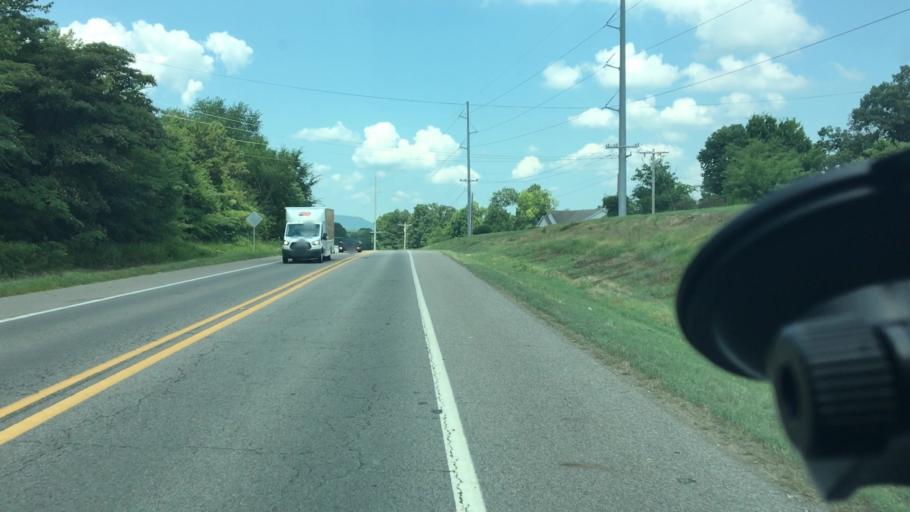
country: US
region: Arkansas
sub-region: Logan County
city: Paris
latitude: 35.2941
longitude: -93.6468
